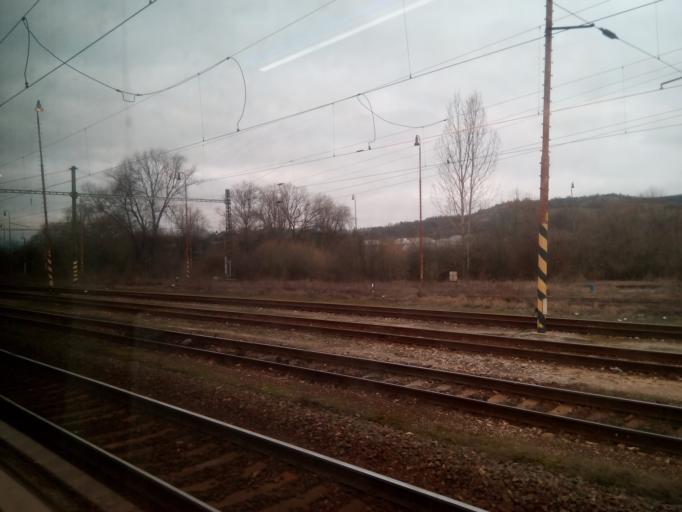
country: SK
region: Zilinsky
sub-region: Okres Liptovsky Mikulas
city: Liptovsky Mikulas
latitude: 49.0926
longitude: 19.6042
